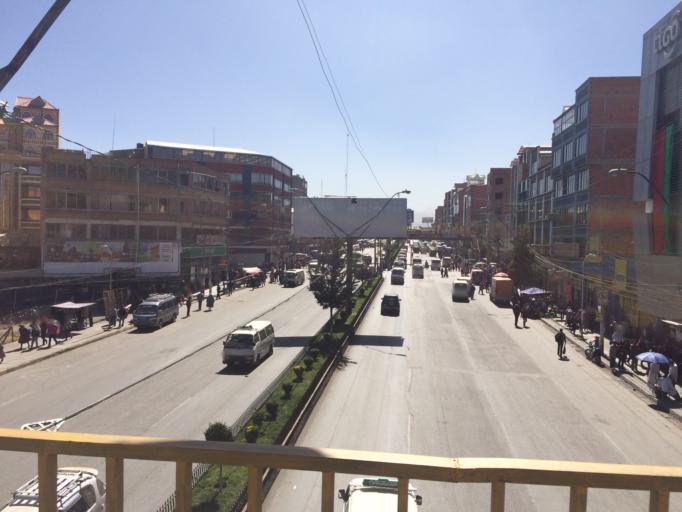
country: BO
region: La Paz
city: La Paz
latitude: -16.5083
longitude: -68.1642
